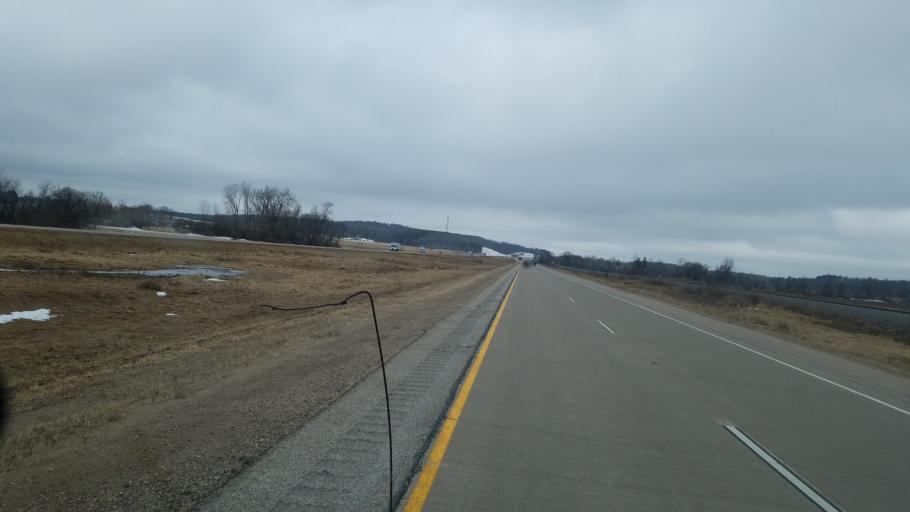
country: US
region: Wisconsin
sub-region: Portage County
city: Amherst
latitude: 44.4026
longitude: -89.2203
